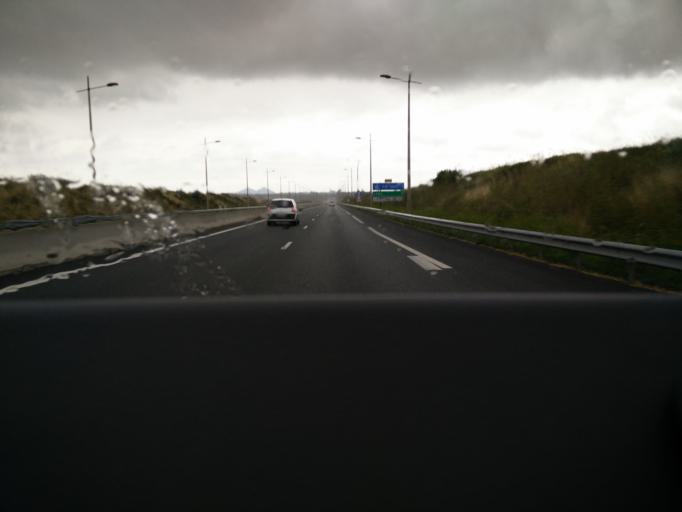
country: FR
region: Nord-Pas-de-Calais
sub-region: Departement du Pas-de-Calais
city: Sains-en-Gohelle
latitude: 50.4353
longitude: 2.6790
